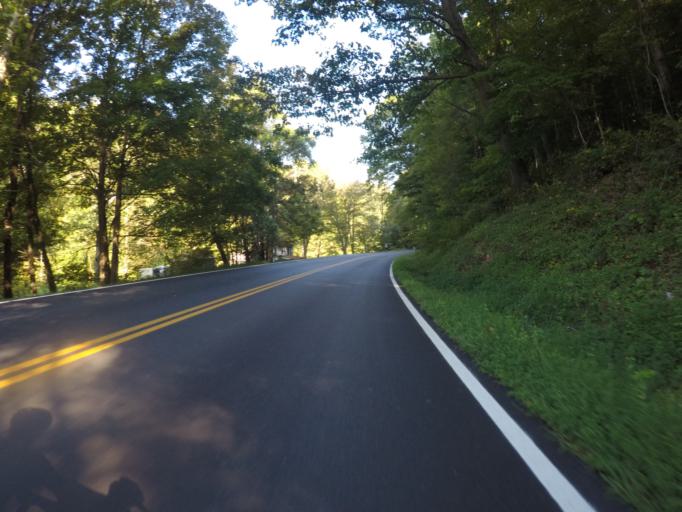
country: US
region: Kentucky
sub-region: Boyd County
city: Catlettsburg
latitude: 38.4229
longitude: -82.6267
